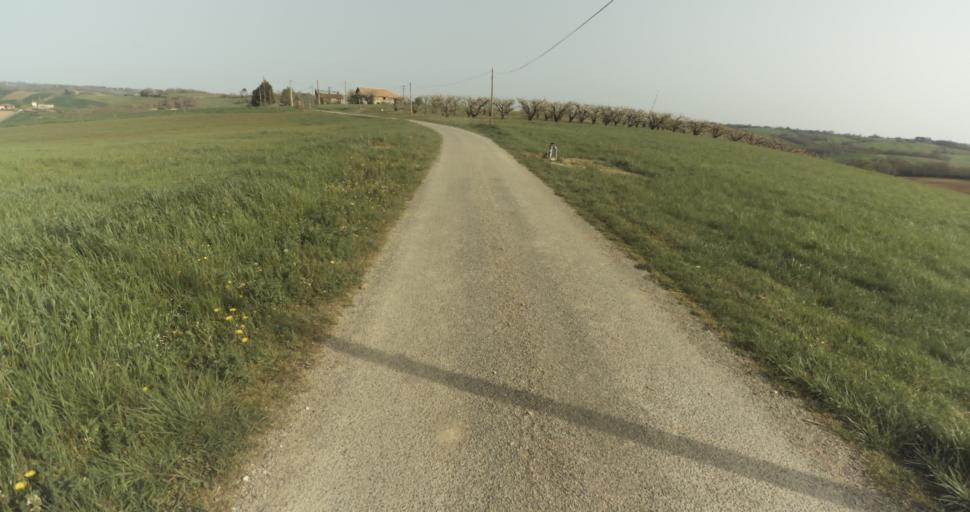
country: FR
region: Midi-Pyrenees
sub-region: Departement du Tarn-et-Garonne
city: Moissac
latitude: 44.1602
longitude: 1.0251
